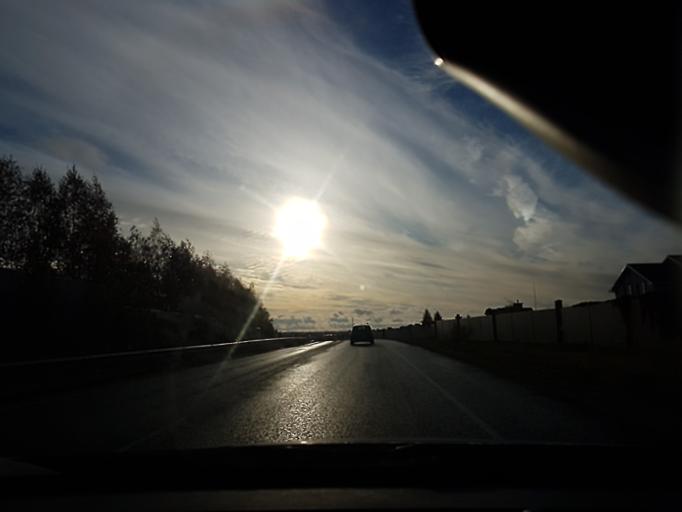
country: RU
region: Moskovskaya
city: Rozhdestveno
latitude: 55.8236
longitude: 37.0460
